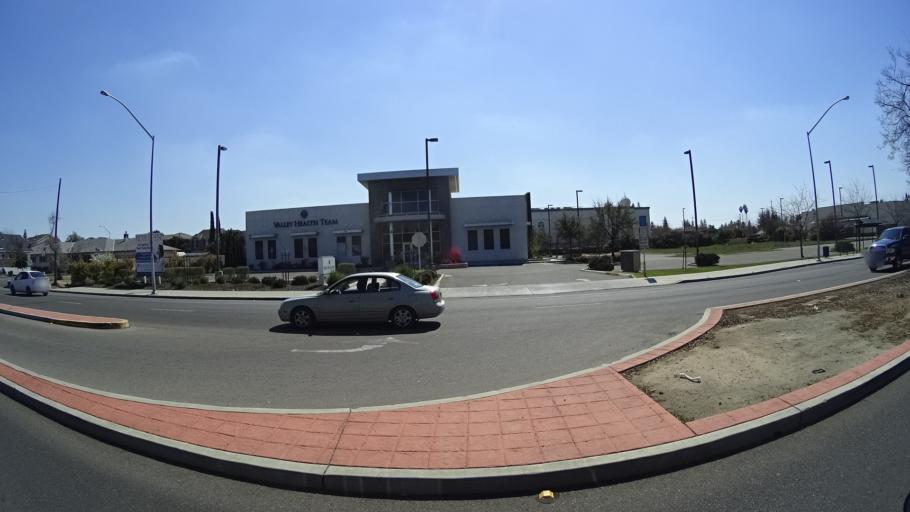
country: US
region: California
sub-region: Fresno County
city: West Park
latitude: 36.7937
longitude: -119.8785
